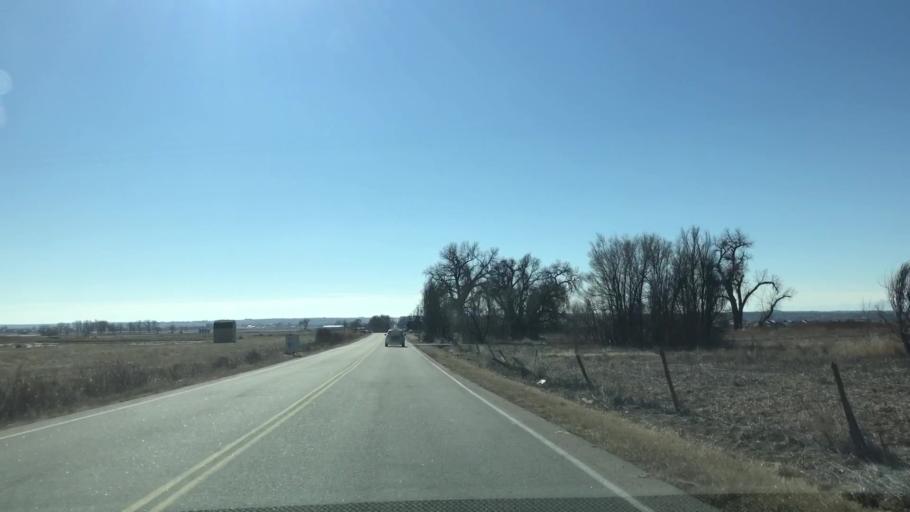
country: US
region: Colorado
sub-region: Weld County
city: Windsor
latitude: 40.5215
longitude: -104.9443
